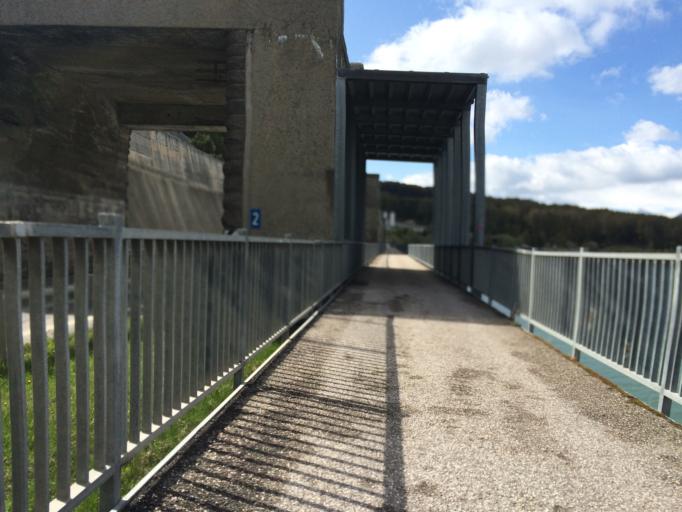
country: IT
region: Trentino-Alto Adige
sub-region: Bolzano
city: Curon Venosta
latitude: 46.7879
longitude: 10.5415
